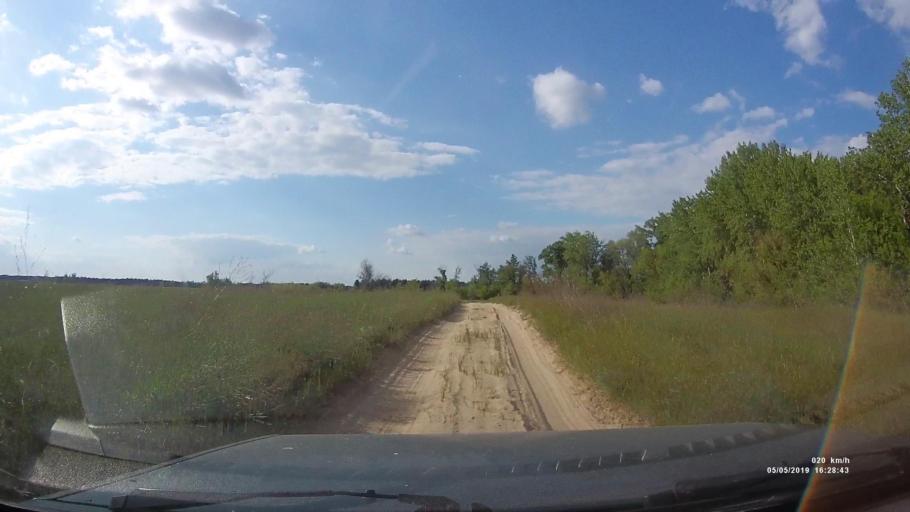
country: RU
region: Rostov
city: Ust'-Donetskiy
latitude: 47.7684
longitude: 41.0155
